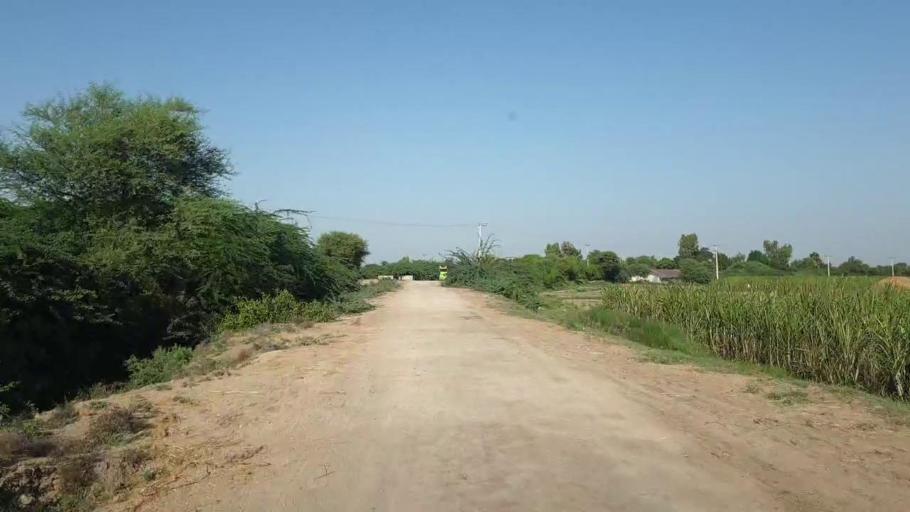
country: PK
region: Sindh
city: Badin
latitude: 24.6087
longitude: 68.9283
